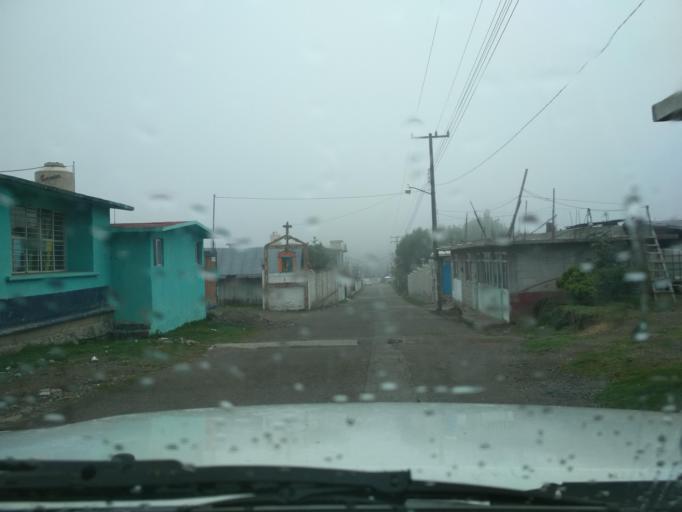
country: MX
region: Veracruz
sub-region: Mariano Escobedo
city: San Isidro el Berro
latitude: 18.9259
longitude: -97.2060
